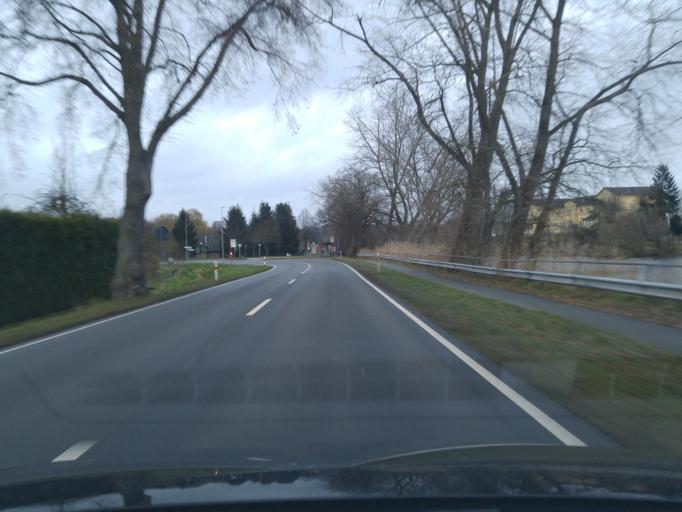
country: DE
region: Schleswig-Holstein
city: Lauenburg
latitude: 53.3594
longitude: 10.5618
